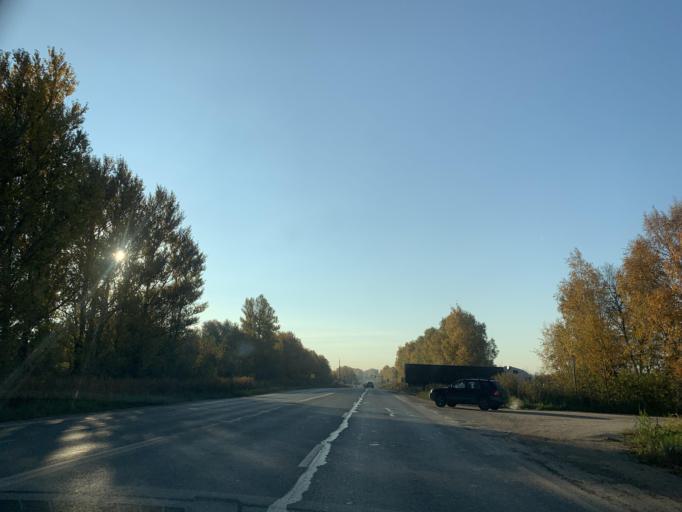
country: RU
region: Jaroslavl
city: Konstantinovskiy
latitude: 57.7373
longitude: 39.7317
